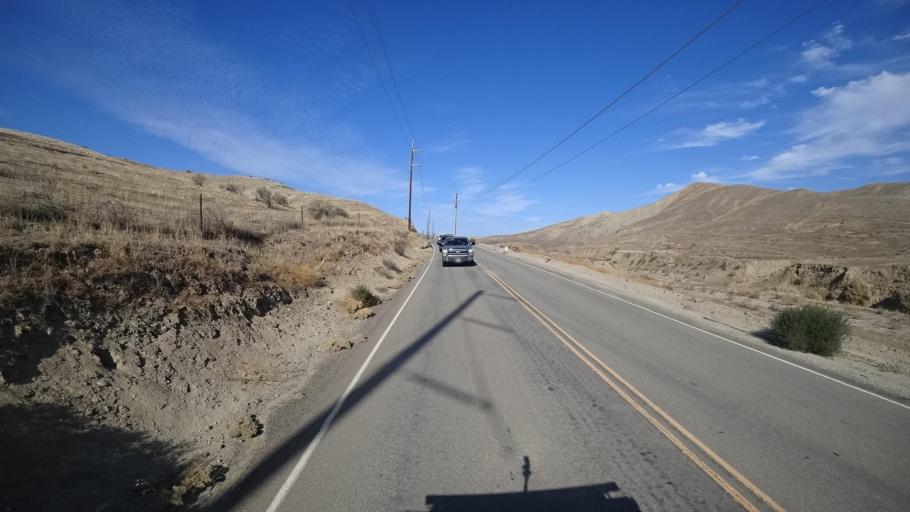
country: US
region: California
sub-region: Kern County
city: Oildale
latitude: 35.5500
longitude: -118.9587
